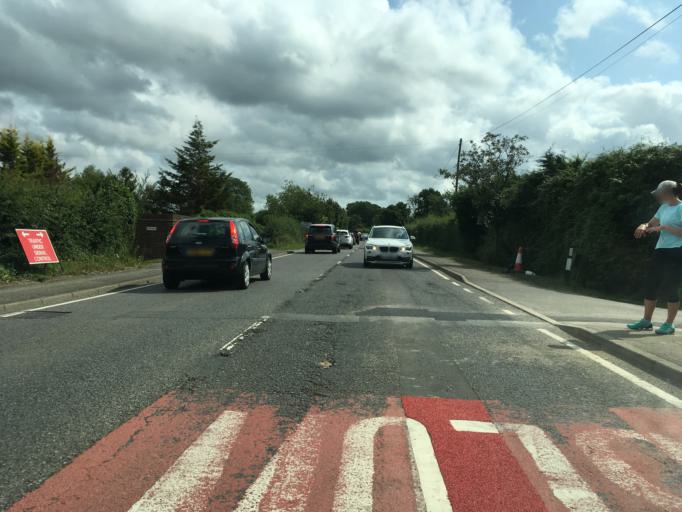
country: GB
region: England
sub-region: Kent
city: Tenterden
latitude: 51.0952
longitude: 0.6890
